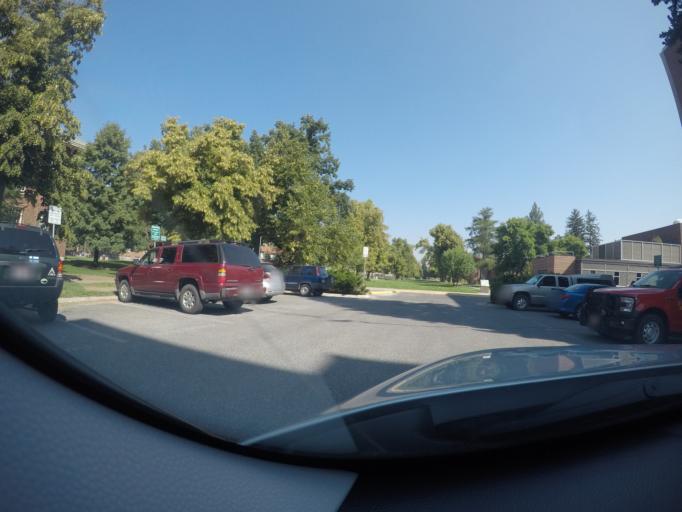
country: US
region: Montana
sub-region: Missoula County
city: Missoula
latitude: 46.8583
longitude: -113.9869
